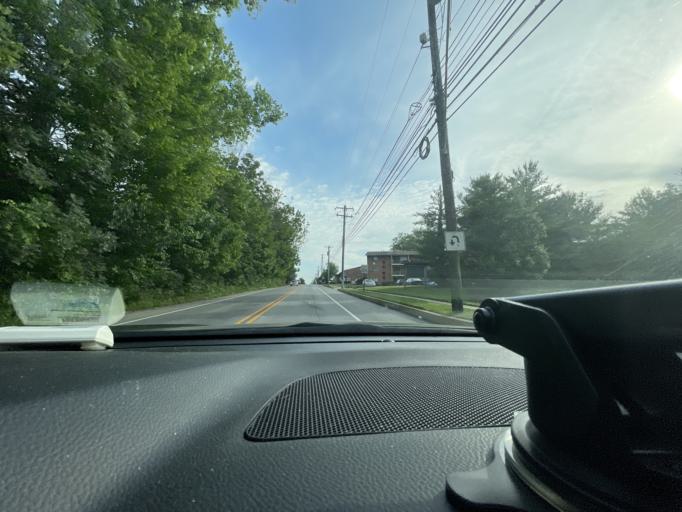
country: US
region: Pennsylvania
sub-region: Montgomery County
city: Plymouth Meeting
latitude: 40.0998
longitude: -75.2814
